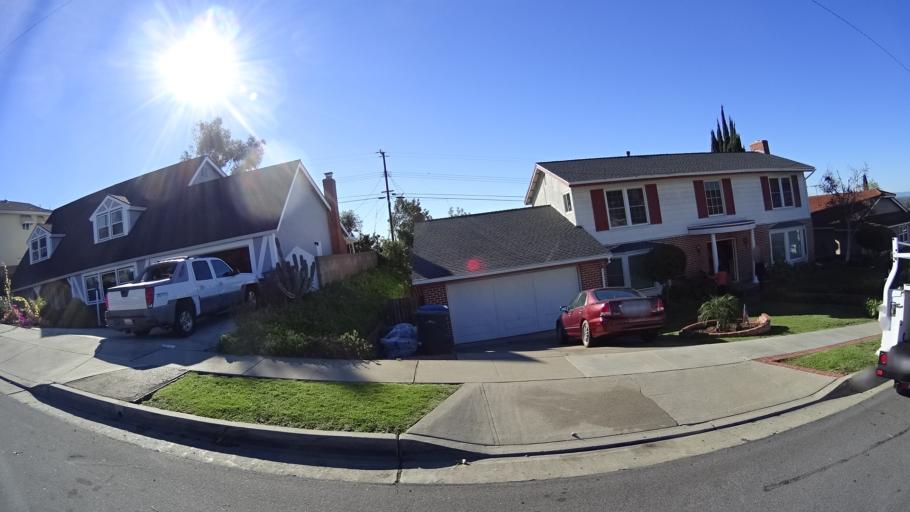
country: US
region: California
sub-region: Orange County
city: La Habra
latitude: 33.9440
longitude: -117.9280
